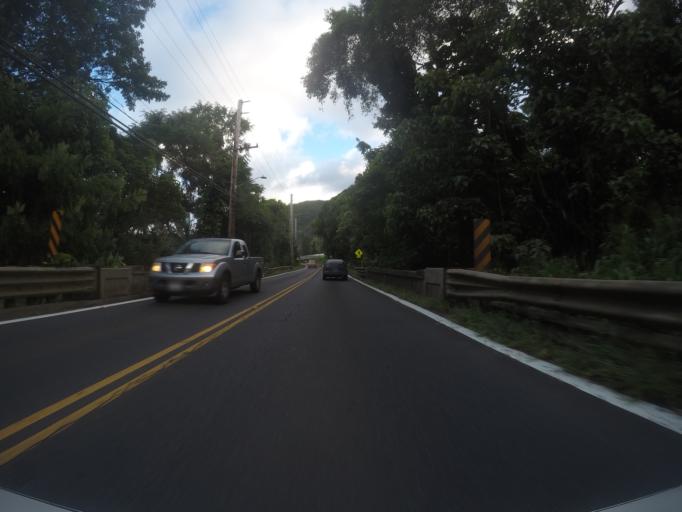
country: US
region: Hawaii
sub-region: Honolulu County
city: Ka'a'awa
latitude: 21.5086
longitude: -157.8551
